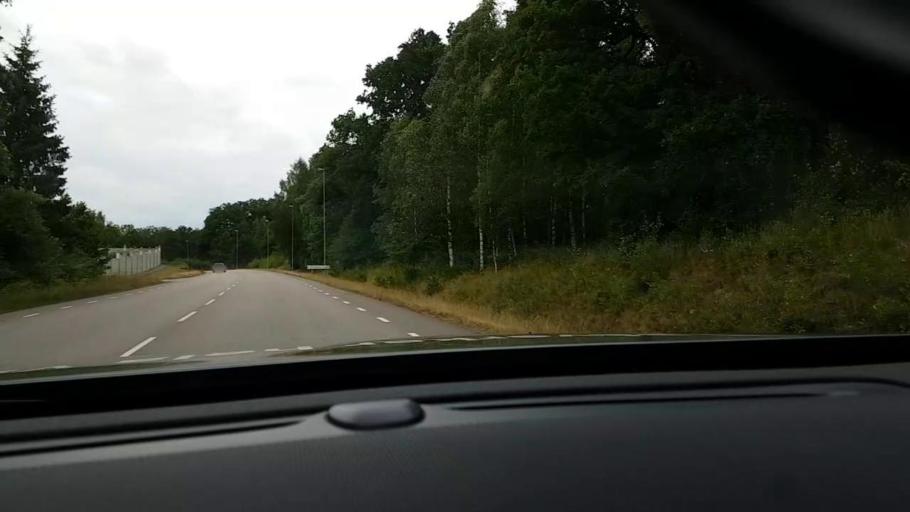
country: SE
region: Skane
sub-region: Hassleholms Kommun
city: Hassleholm
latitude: 56.1677
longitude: 13.7450
